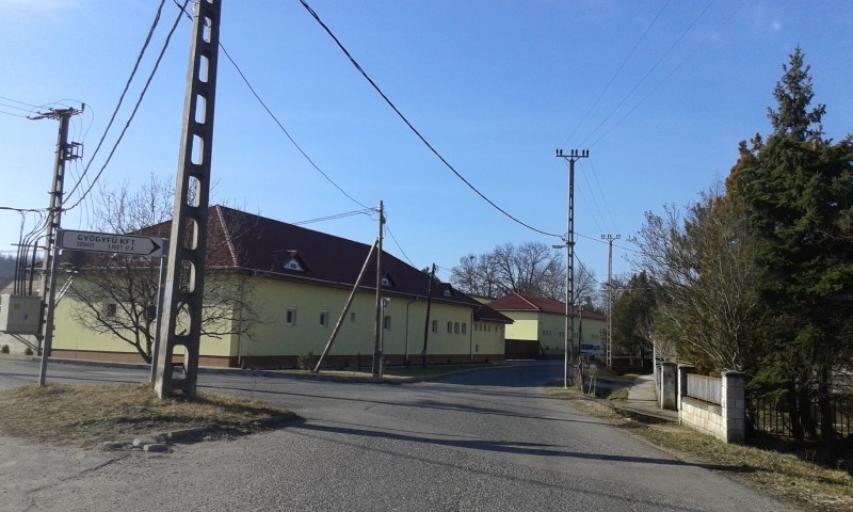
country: HU
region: Pest
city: Soskut
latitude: 47.4038
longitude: 18.8262
